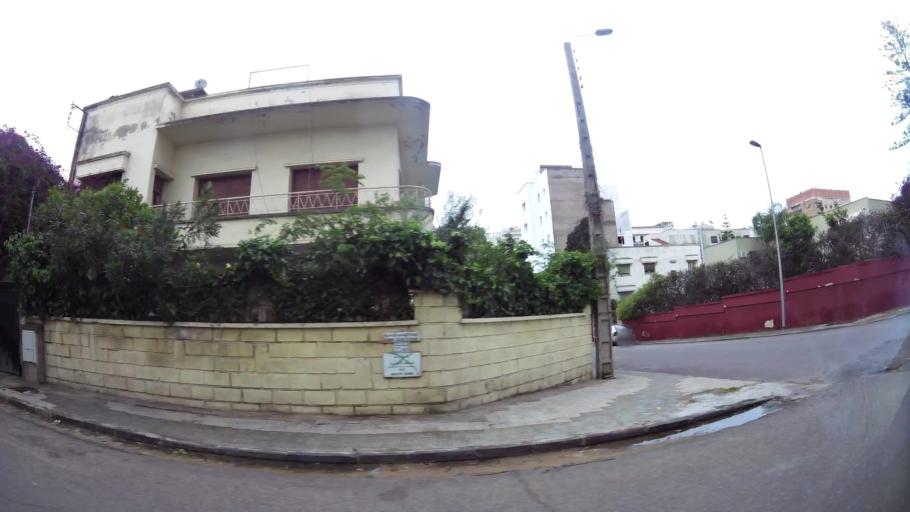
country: MA
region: Grand Casablanca
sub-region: Casablanca
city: Casablanca
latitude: 33.5714
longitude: -7.6204
